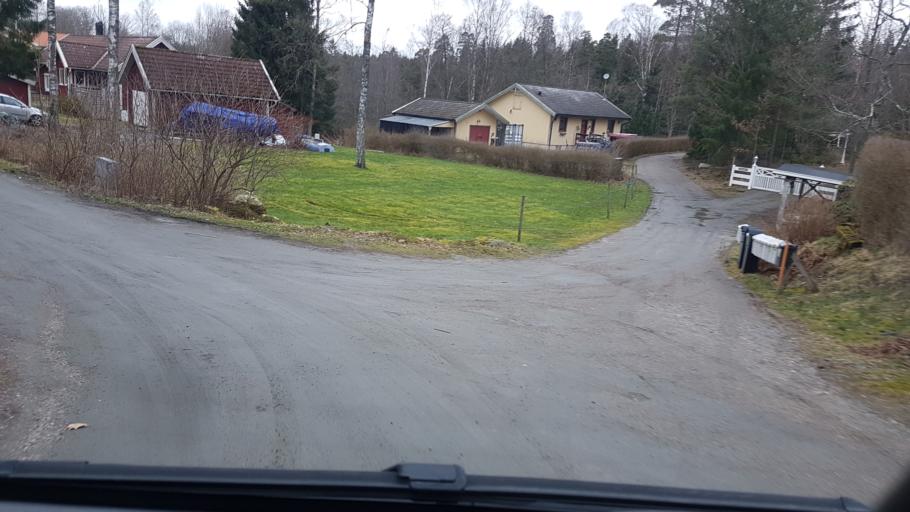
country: SE
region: Vaestra Goetaland
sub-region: Lerums Kommun
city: Stenkullen
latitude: 57.7955
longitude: 12.3958
